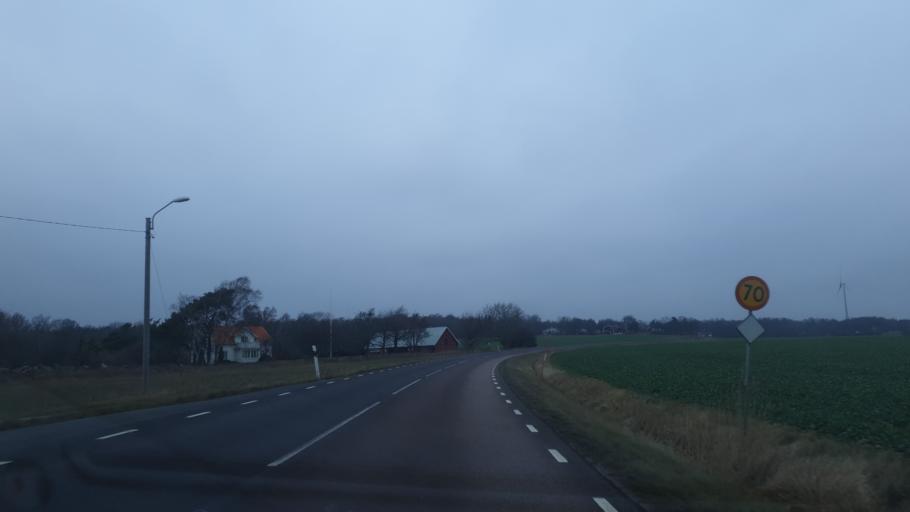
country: SE
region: Blekinge
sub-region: Karlskrona Kommun
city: Sturko
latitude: 56.1755
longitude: 15.7220
